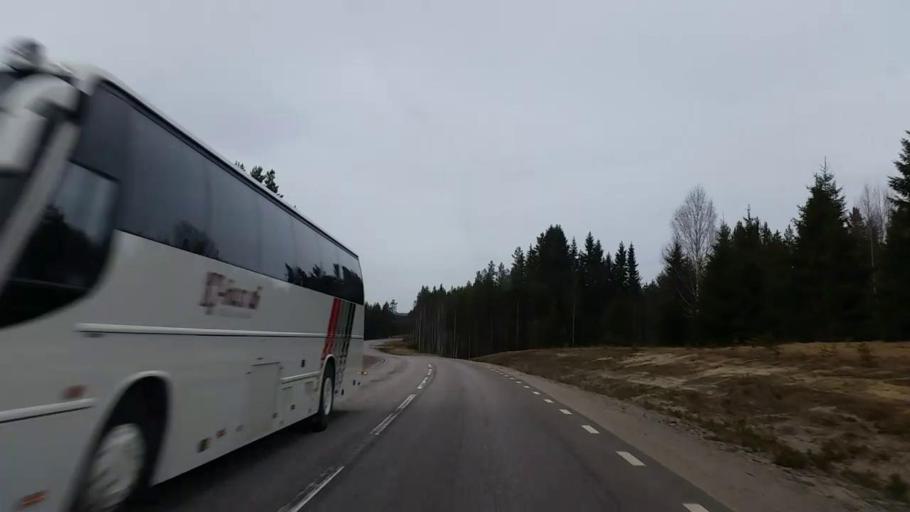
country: SE
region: Gaevleborg
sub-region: Ovanakers Kommun
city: Edsbyn
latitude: 61.1763
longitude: 15.8830
